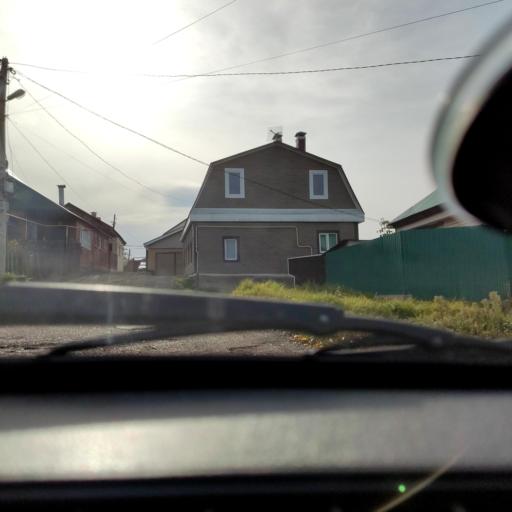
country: RU
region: Bashkortostan
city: Ufa
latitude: 54.7280
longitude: 55.9172
